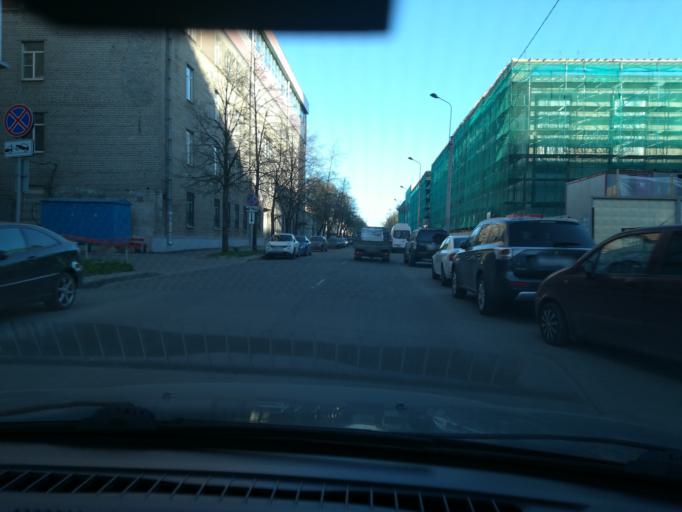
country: RU
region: St.-Petersburg
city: Vasyl'evsky Ostrov
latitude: 59.9391
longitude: 30.2525
